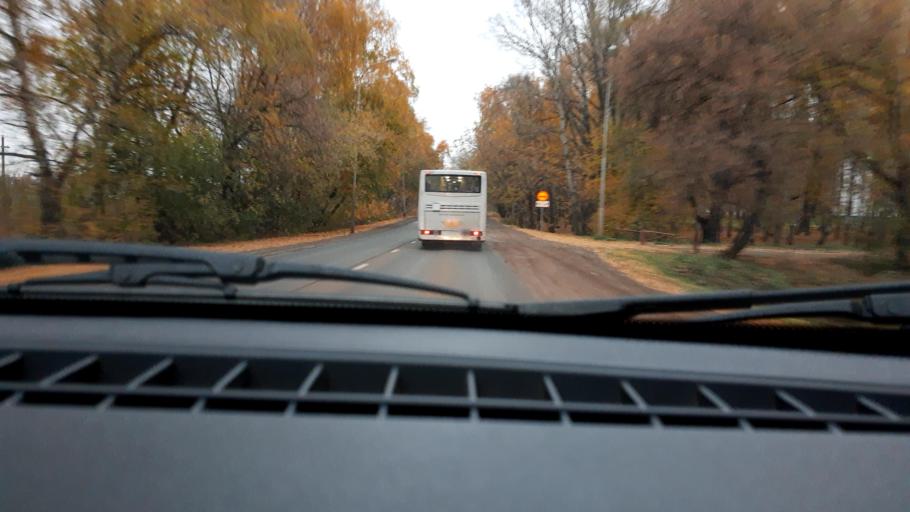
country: RU
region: Bashkortostan
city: Avdon
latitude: 54.7182
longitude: 55.8088
